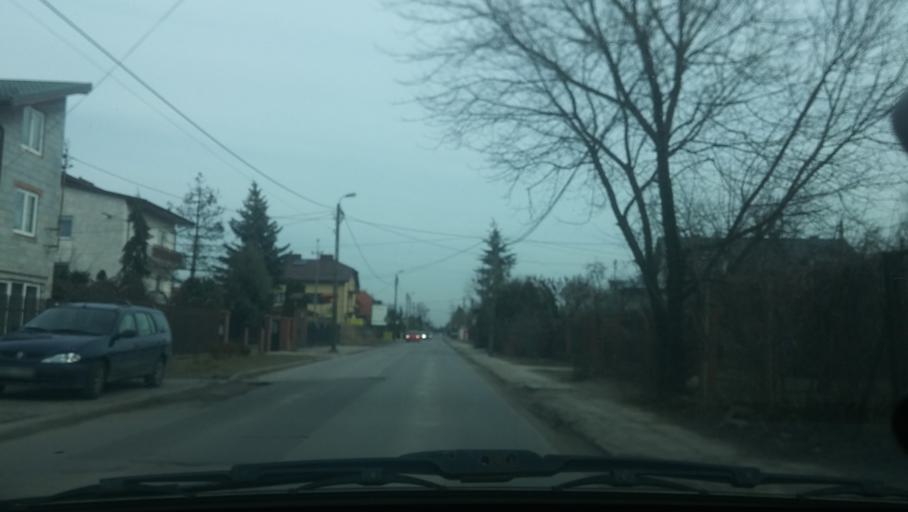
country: PL
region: Masovian Voivodeship
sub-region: Powiat wolominski
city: Marki
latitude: 52.3090
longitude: 21.1068
